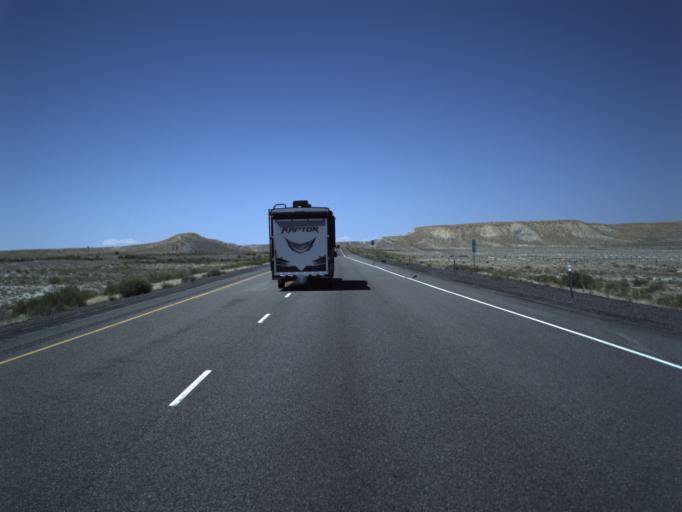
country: US
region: Utah
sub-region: Grand County
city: Moab
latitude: 38.9428
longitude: -109.6225
